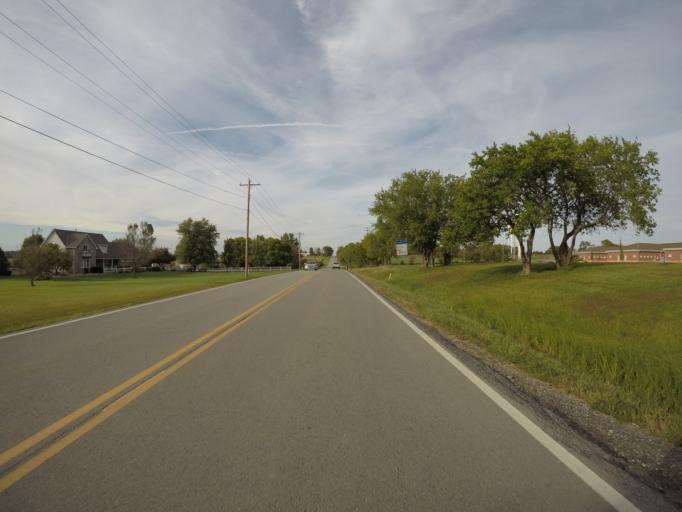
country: US
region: Kansas
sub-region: Douglas County
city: Baldwin City
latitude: 38.7774
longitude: -95.2050
